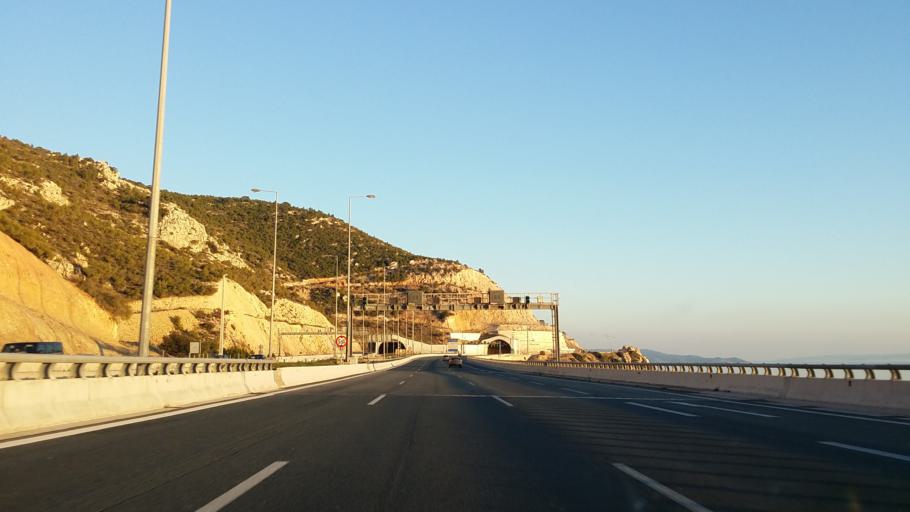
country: GR
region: Attica
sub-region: Nomarchia Dytikis Attikis
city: Megara
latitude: 37.9765
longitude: 23.2870
